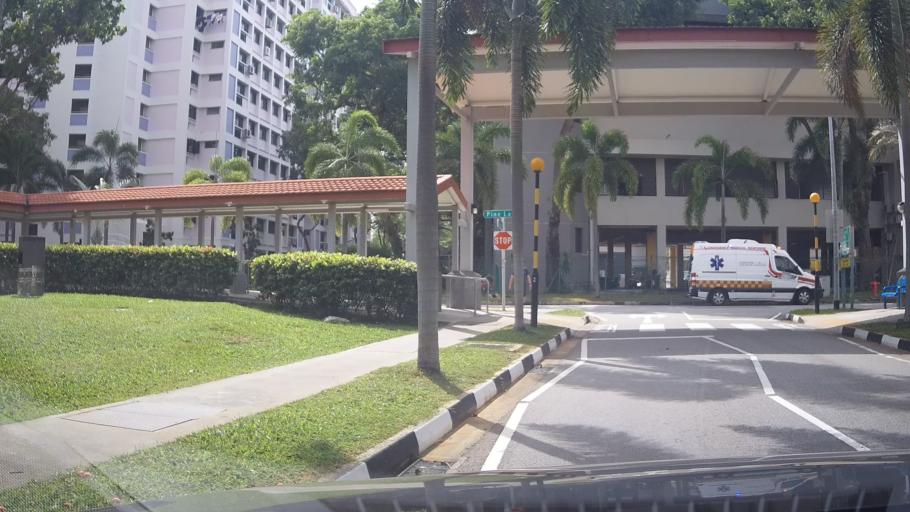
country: SG
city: Singapore
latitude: 1.3096
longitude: 103.8831
